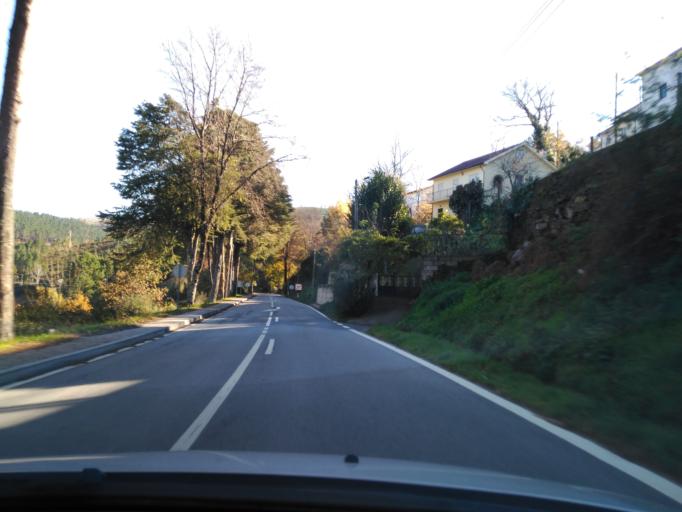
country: PT
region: Braga
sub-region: Cabeceiras de Basto
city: Cabeceiras de Basto
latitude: 41.6737
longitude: -7.9583
